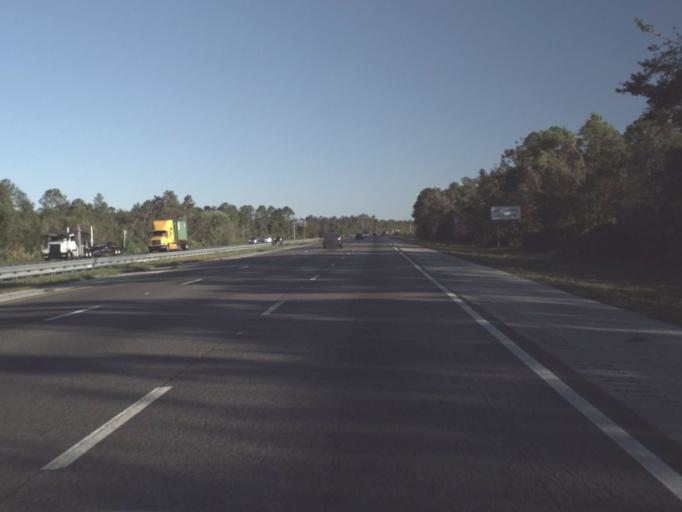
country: US
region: Florida
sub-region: Flagler County
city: Palm Coast
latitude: 29.5390
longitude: -81.2091
